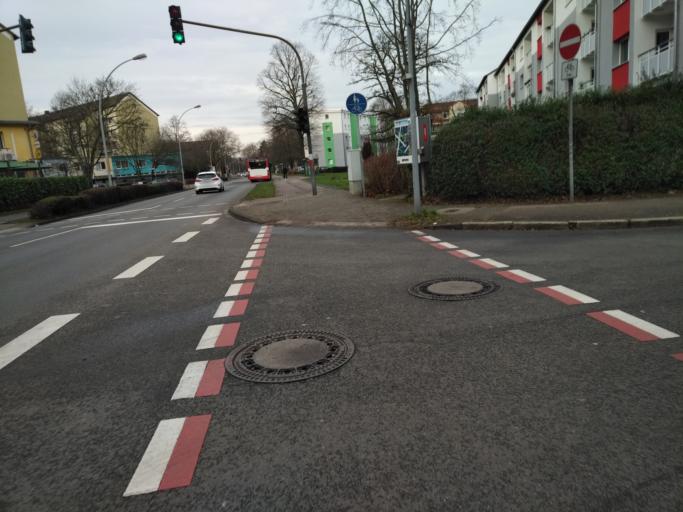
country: DE
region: North Rhine-Westphalia
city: Opladen
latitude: 51.0437
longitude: 7.0277
